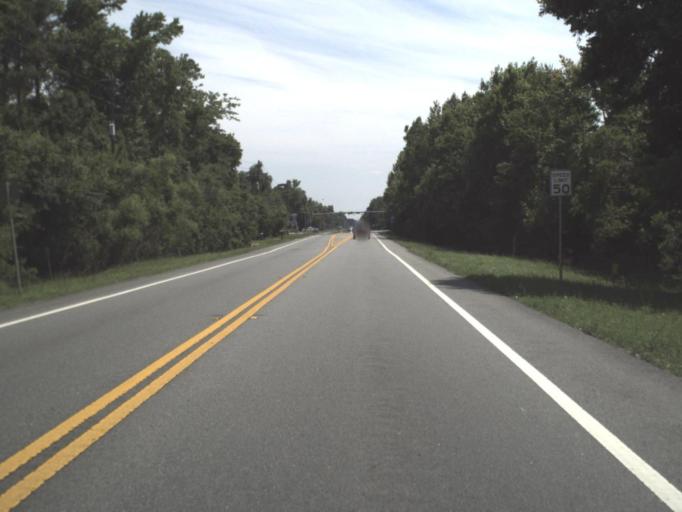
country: US
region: Florida
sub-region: Nassau County
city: Yulee
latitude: 30.5210
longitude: -81.6225
